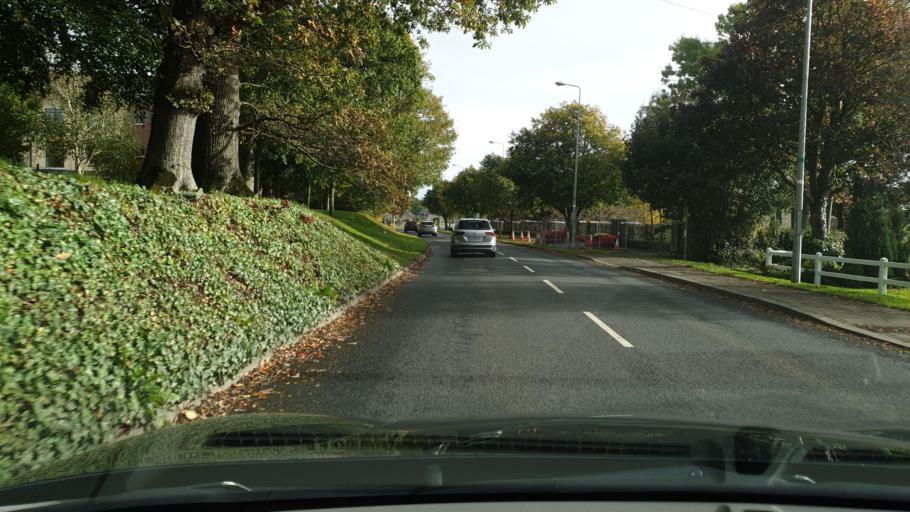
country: IE
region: Leinster
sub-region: An Mhi
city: Ratoath
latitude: 53.5100
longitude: -6.4739
